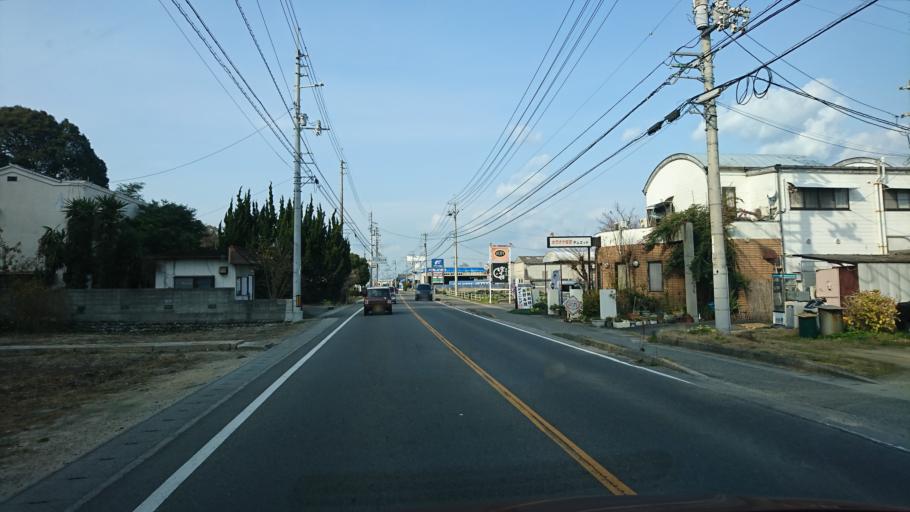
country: JP
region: Ehime
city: Saijo
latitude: 34.0305
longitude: 133.0363
